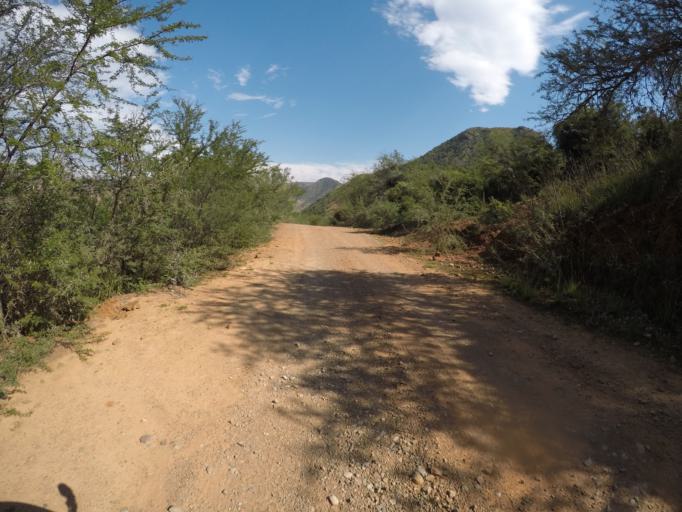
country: ZA
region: Eastern Cape
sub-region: Cacadu District Municipality
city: Kareedouw
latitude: -33.6591
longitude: 24.3992
